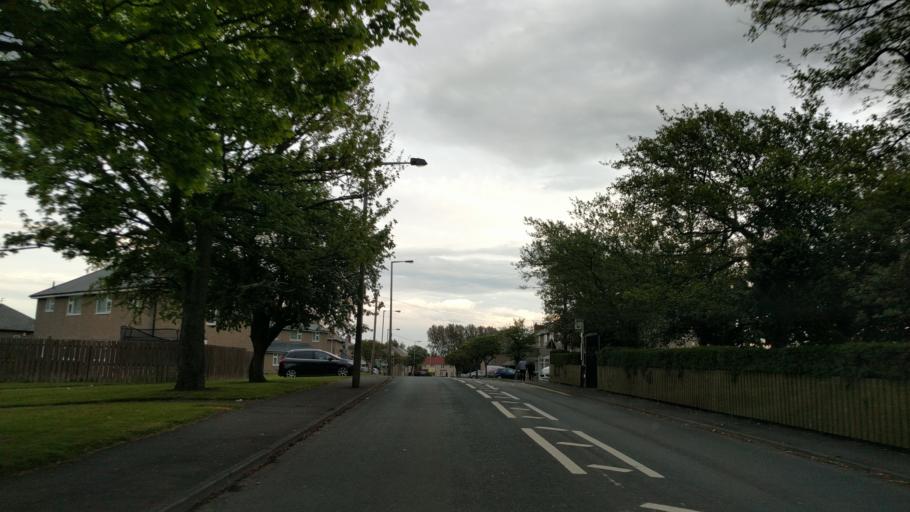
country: GB
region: England
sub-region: Northumberland
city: Cramlington
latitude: 55.0840
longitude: -1.5731
